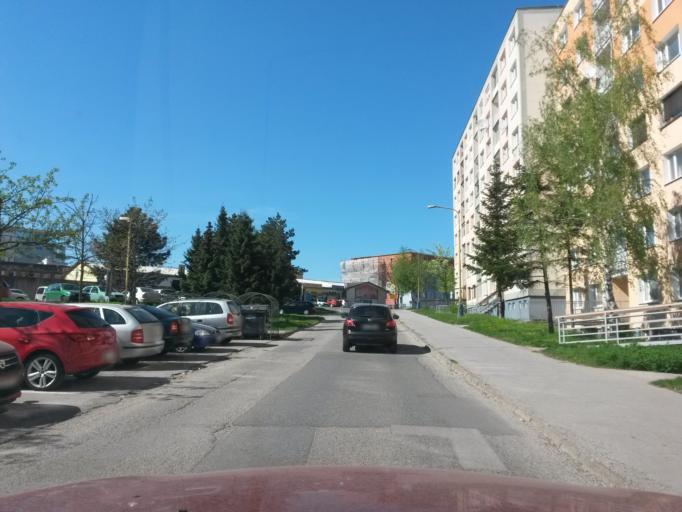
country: SK
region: Kosicky
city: Kosice
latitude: 48.7075
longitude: 21.2492
